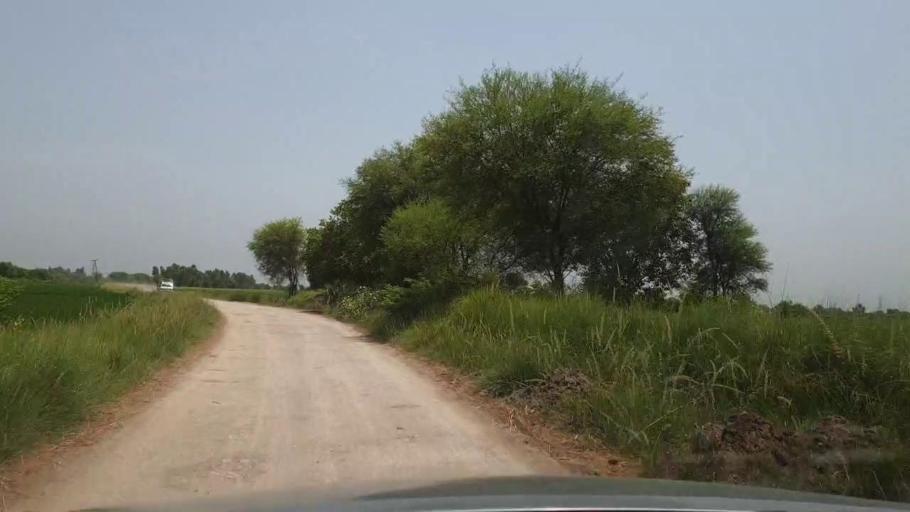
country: PK
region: Sindh
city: Ratodero
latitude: 27.8020
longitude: 68.3408
